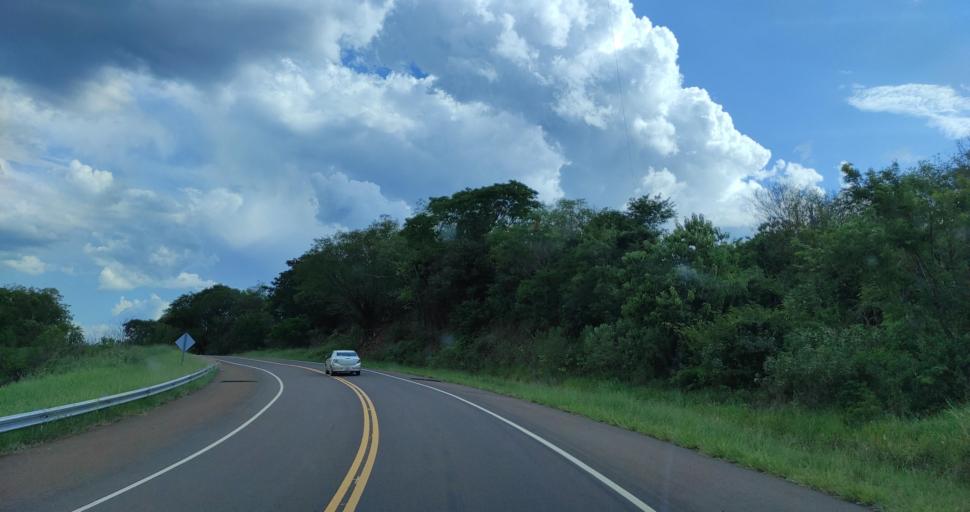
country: AR
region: Misiones
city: Bernardo de Irigoyen
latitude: -26.3004
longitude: -53.8156
